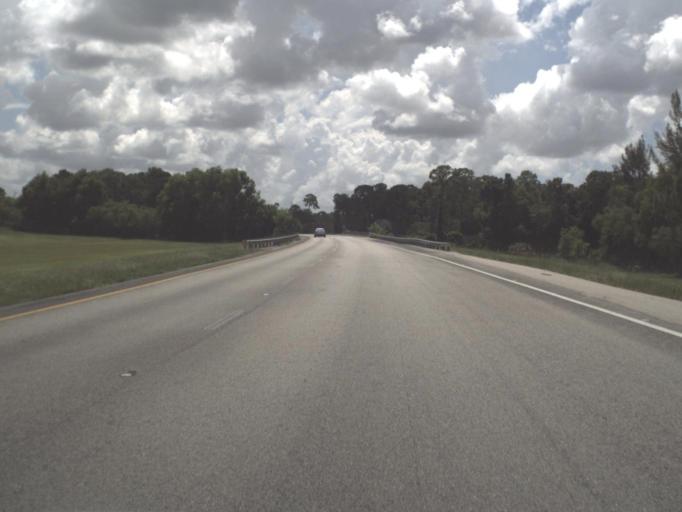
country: US
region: Florida
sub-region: Collier County
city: Golden Gate
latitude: 26.1700
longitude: -81.7325
